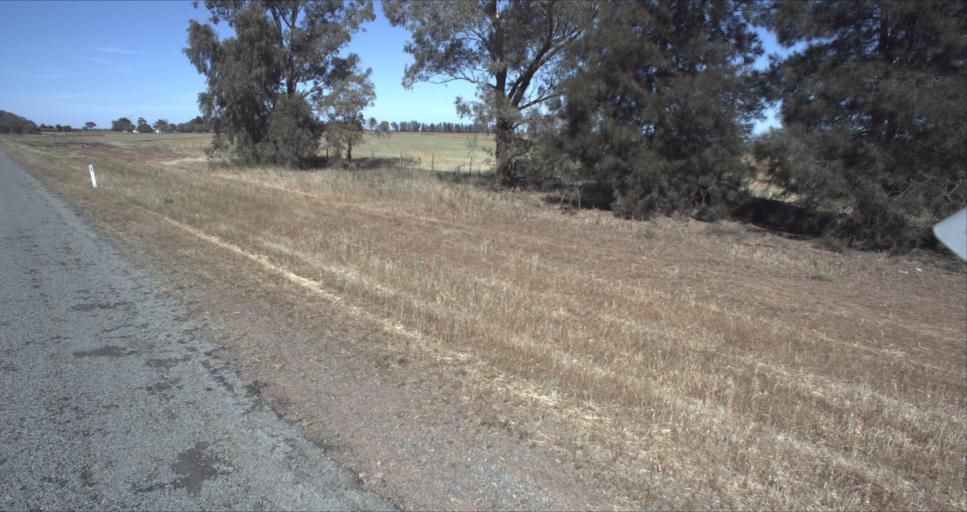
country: AU
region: New South Wales
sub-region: Leeton
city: Leeton
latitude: -34.5367
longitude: 146.3173
